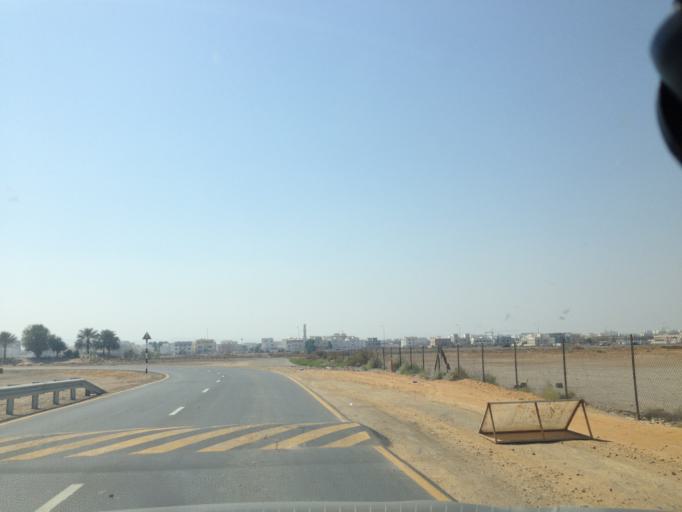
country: OM
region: Muhafazat Masqat
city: As Sib al Jadidah
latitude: 23.6295
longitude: 58.2609
